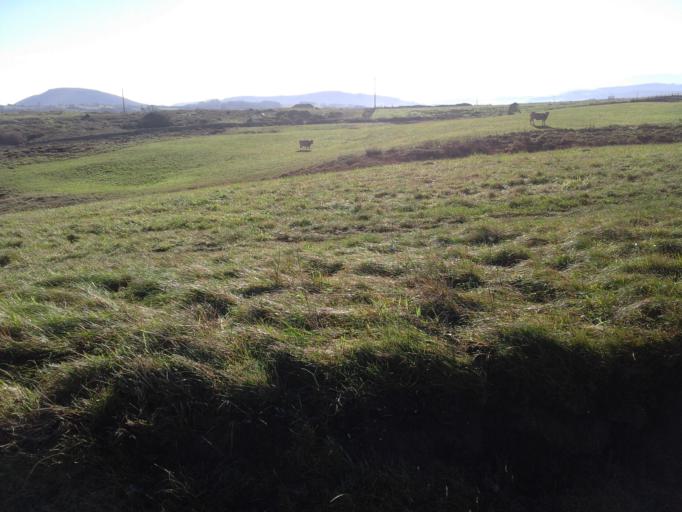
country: ES
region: Cantabria
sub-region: Provincia de Cantabria
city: Arnuero
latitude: 43.5117
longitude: -3.5928
